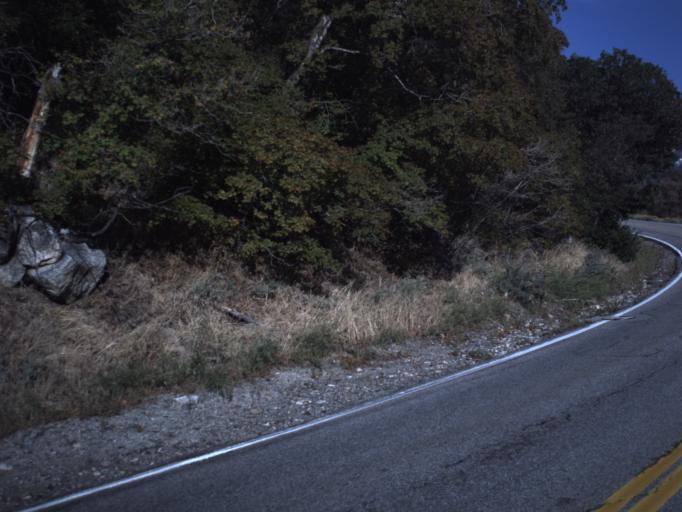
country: US
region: Utah
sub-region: Salt Lake County
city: Granite
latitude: 40.5717
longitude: -111.7679
